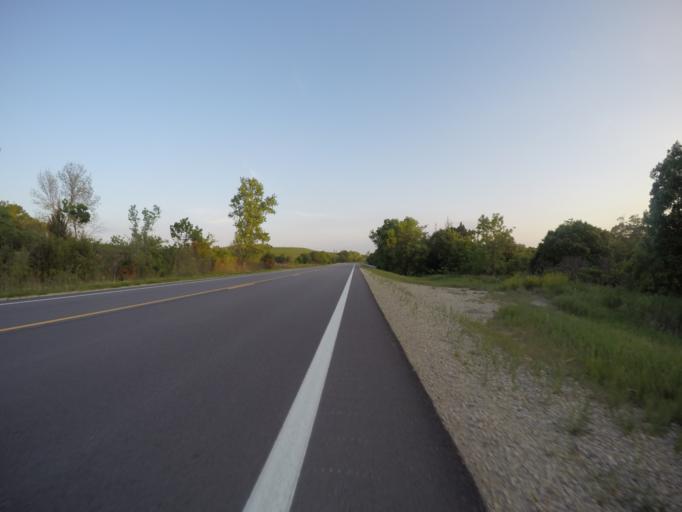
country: US
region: Kansas
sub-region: Riley County
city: Manhattan
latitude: 39.2945
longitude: -96.5568
